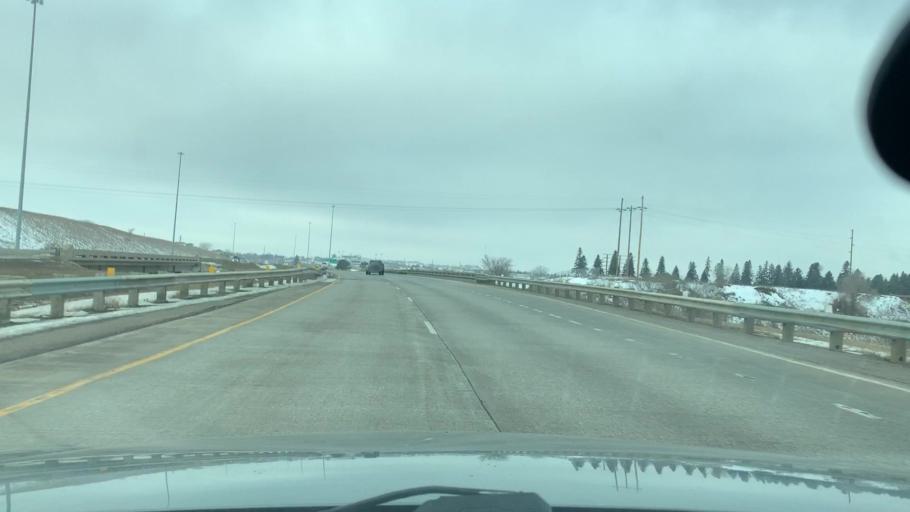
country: US
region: North Dakota
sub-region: Morton County
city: Mandan
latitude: 46.8368
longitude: -100.8683
